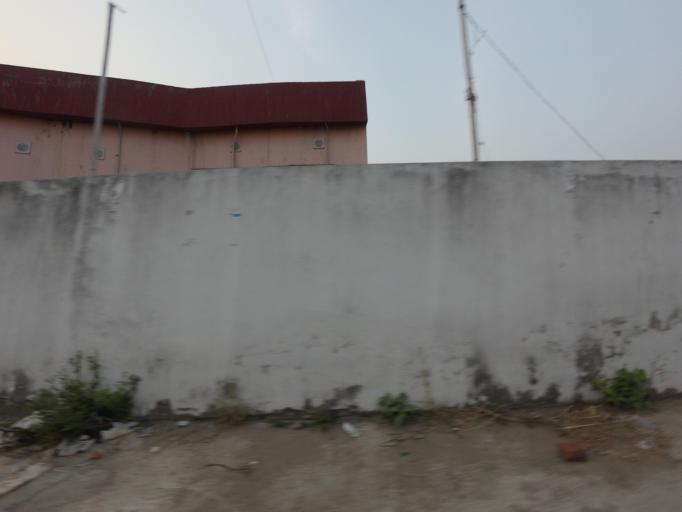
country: NP
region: Western Region
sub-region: Lumbini Zone
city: Bhairahawa
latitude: 27.5023
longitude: 83.4585
